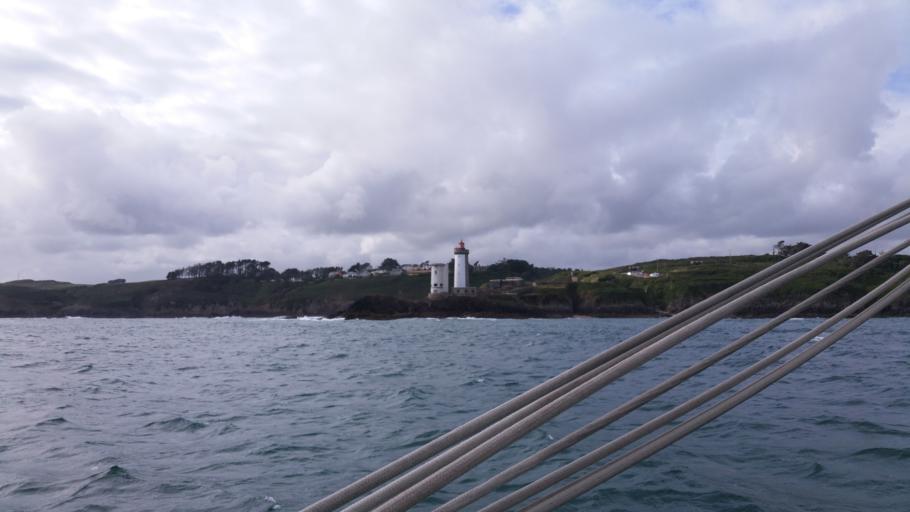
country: FR
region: Brittany
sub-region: Departement du Finistere
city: Plouzane
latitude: 48.3338
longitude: -4.6121
